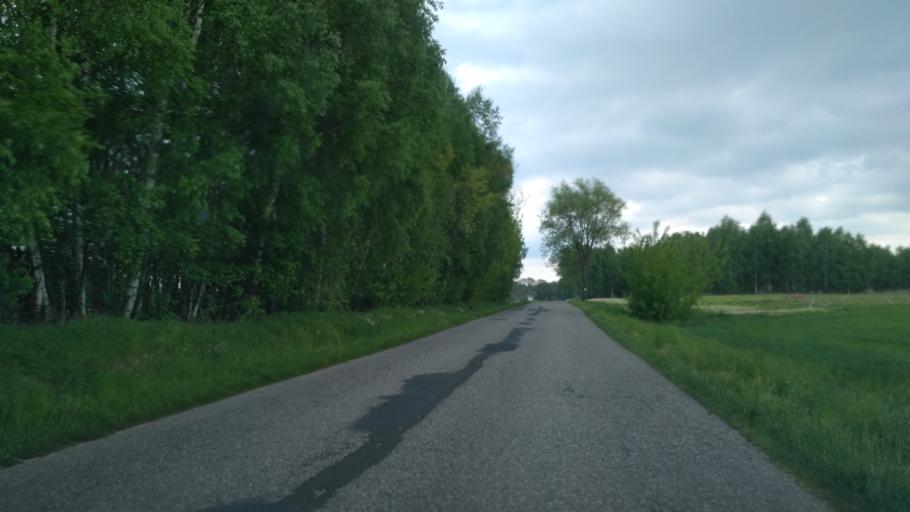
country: PL
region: Lesser Poland Voivodeship
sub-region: Powiat tarnowski
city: Szynwald
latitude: 49.9834
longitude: 21.1357
